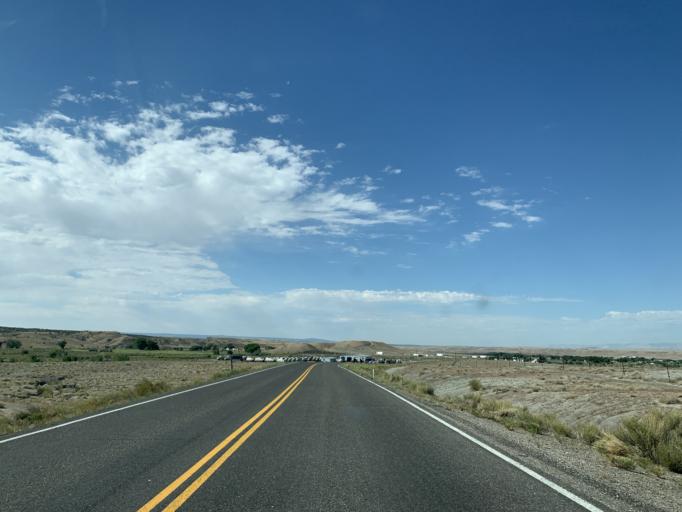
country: US
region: Utah
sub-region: Carbon County
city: Wellington
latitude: 39.5570
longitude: -110.6662
